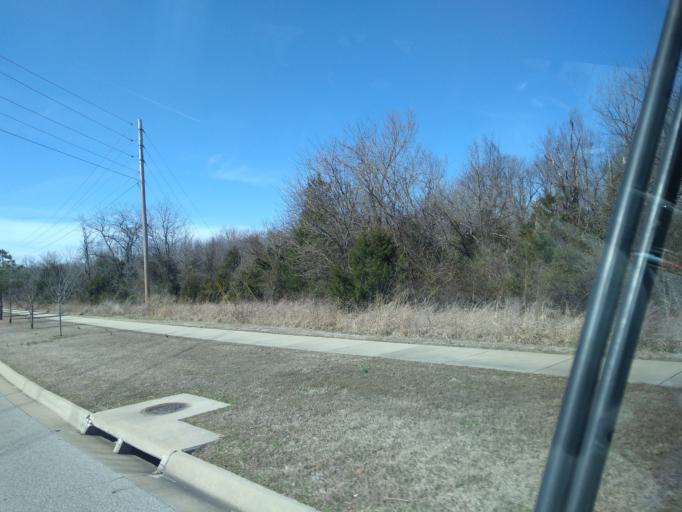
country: US
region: Arkansas
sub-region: Washington County
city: Farmington
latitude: 36.0611
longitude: -94.2321
